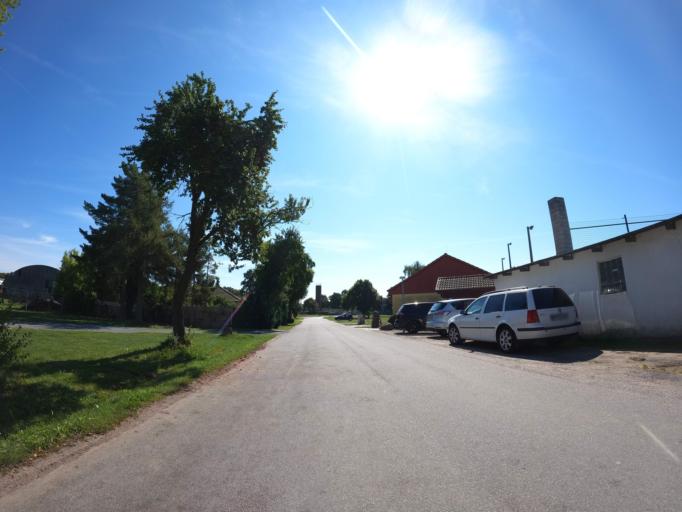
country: DE
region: Mecklenburg-Vorpommern
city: Prohn
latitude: 54.3780
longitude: 13.0219
